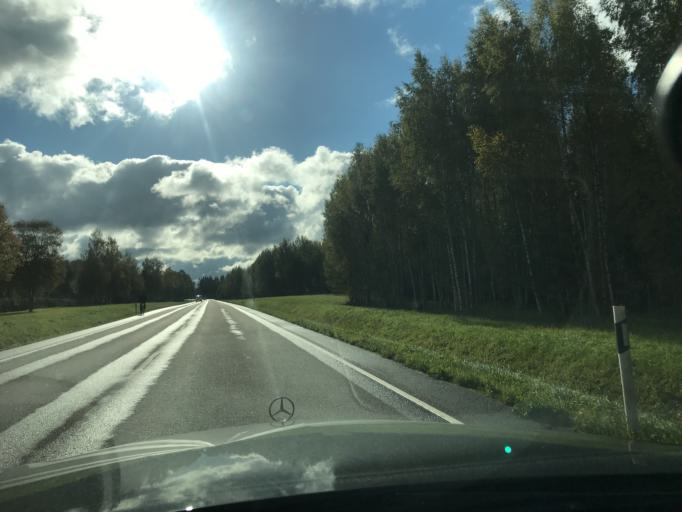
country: EE
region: Valgamaa
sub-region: Torva linn
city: Torva
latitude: 57.9849
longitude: 25.9436
